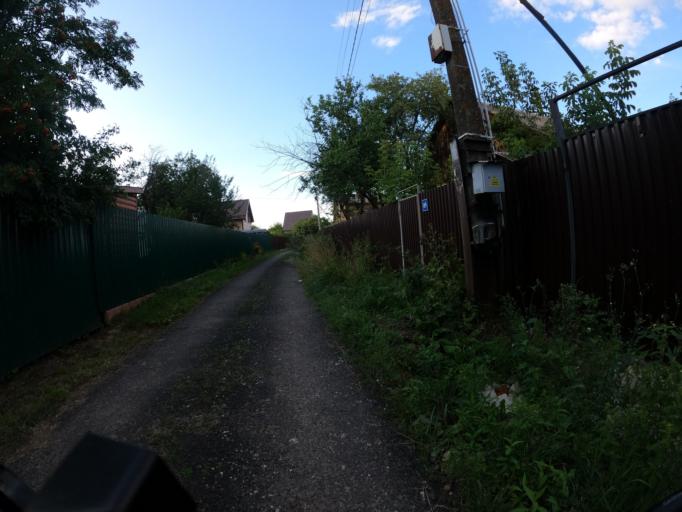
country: RU
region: Moskovskaya
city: Beloozerskiy
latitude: 55.4479
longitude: 38.4998
